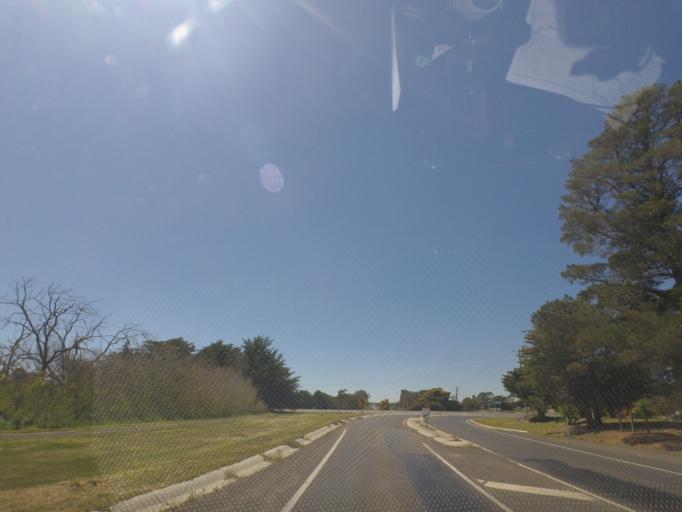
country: AU
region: Victoria
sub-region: Hume
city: Sunbury
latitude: -37.4141
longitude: 144.7479
